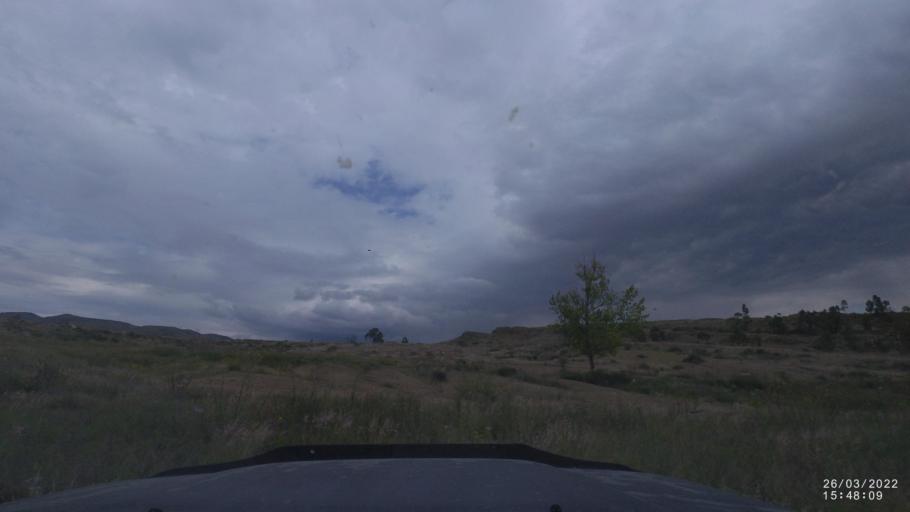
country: BO
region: Cochabamba
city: Cliza
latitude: -17.7467
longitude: -65.8567
